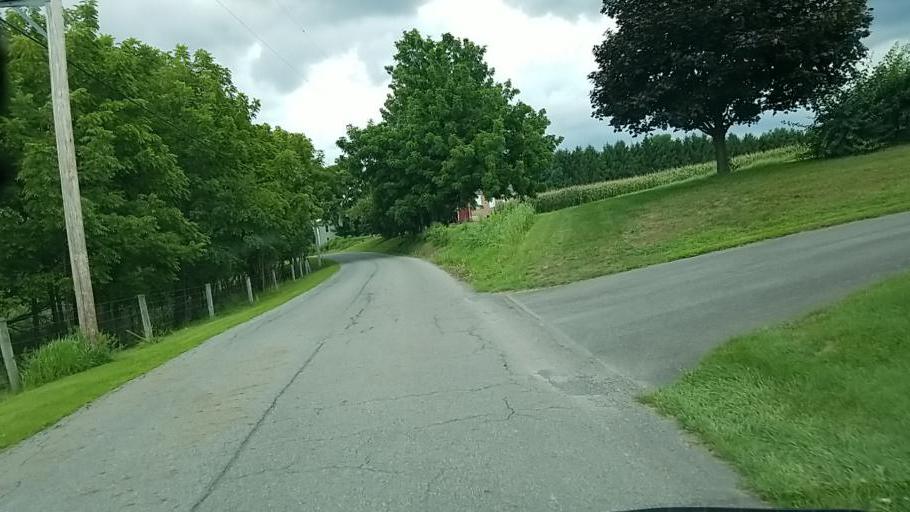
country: US
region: Pennsylvania
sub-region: Dauphin County
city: Elizabethville
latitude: 40.5940
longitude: -76.8020
